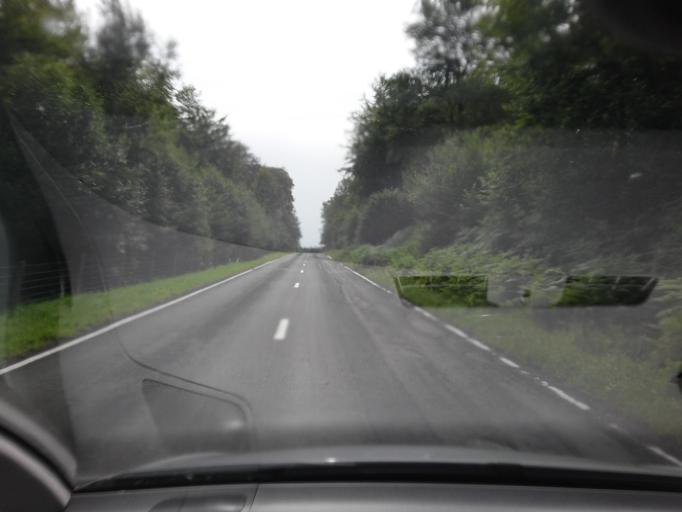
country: BE
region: Wallonia
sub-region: Province du Luxembourg
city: Chiny
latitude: 49.7735
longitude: 5.3548
